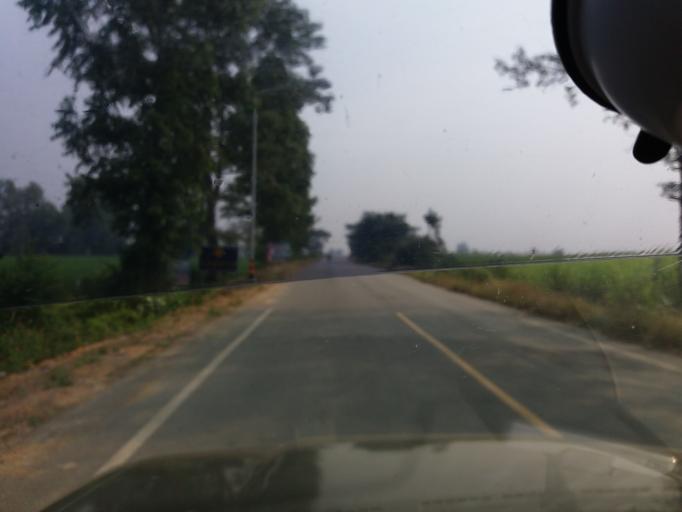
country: TH
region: Suphan Buri
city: Doem Bang Nang Buat
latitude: 14.8524
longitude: 100.1305
